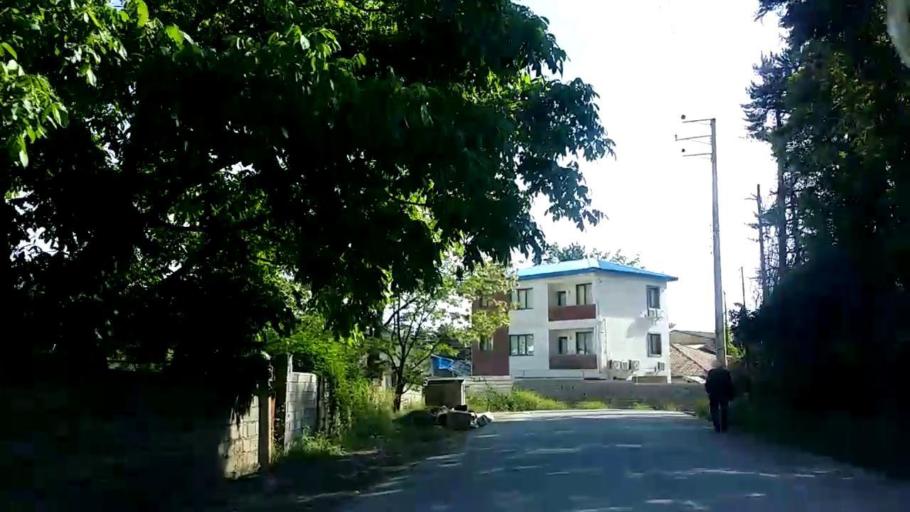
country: IR
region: Mazandaran
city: `Abbasabad
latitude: 36.5042
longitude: 51.1568
